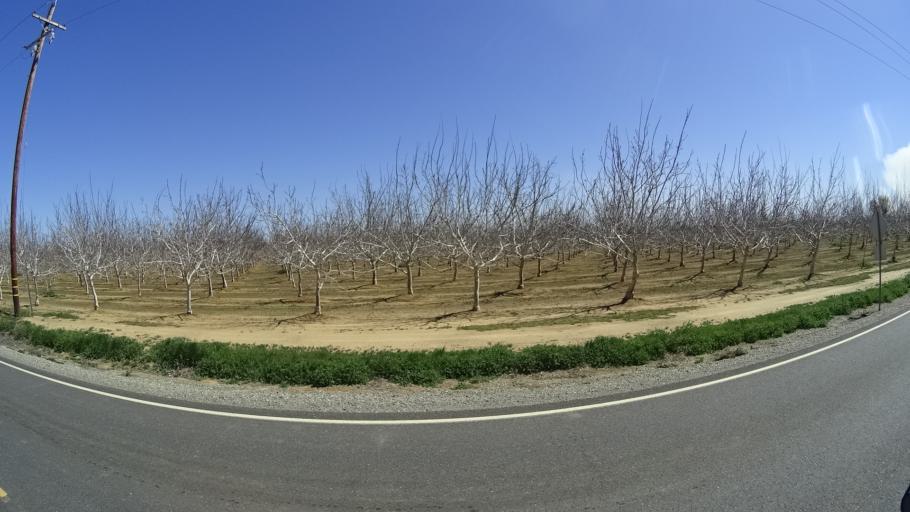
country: US
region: California
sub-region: Glenn County
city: Willows
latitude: 39.5117
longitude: -122.2492
